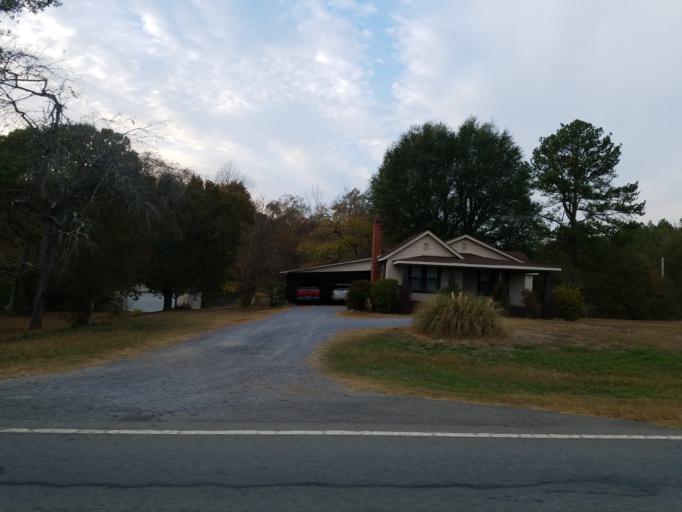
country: US
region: Georgia
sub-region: Gordon County
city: Calhoun
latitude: 34.5988
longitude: -84.9278
